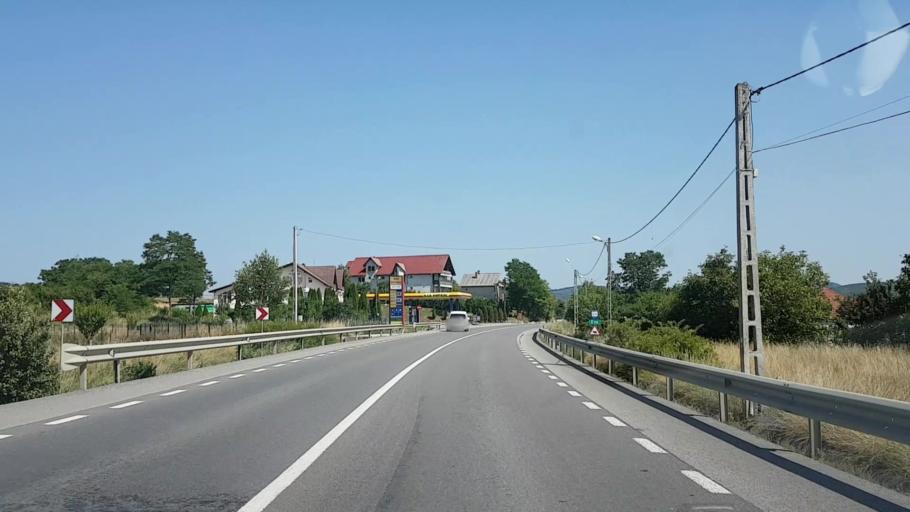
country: RO
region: Bistrita-Nasaud
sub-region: Comuna Uriu
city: Cristestii Ciceului
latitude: 47.1817
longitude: 24.1381
